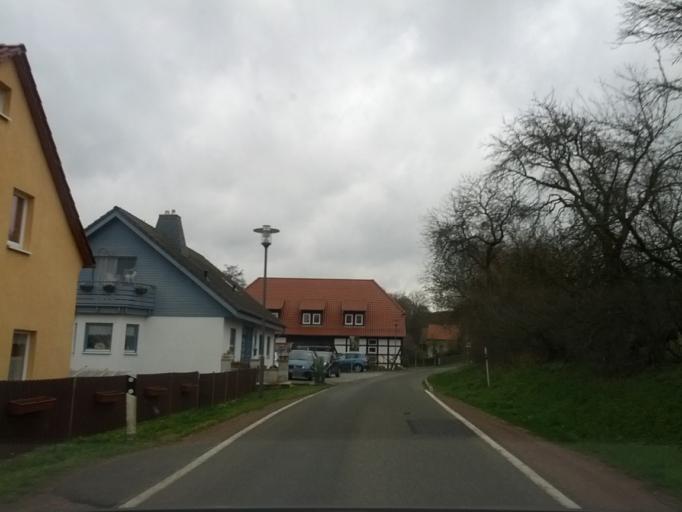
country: DE
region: Thuringia
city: Haina
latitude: 51.0256
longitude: 10.4664
